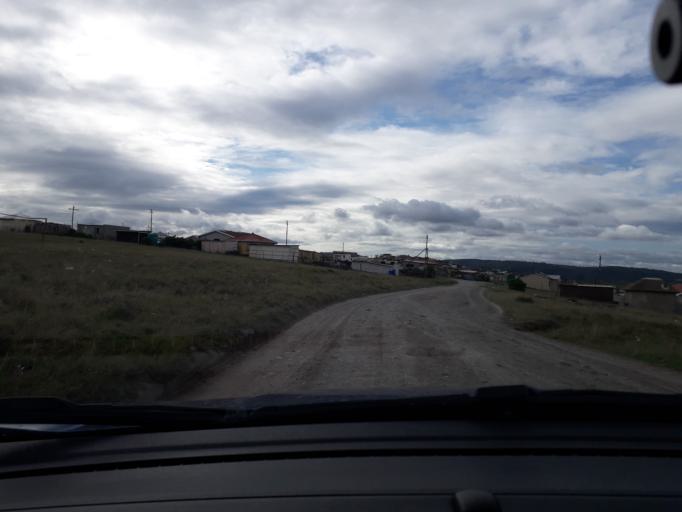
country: ZA
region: Eastern Cape
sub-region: Buffalo City Metropolitan Municipality
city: East London
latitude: -32.8533
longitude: 27.9841
